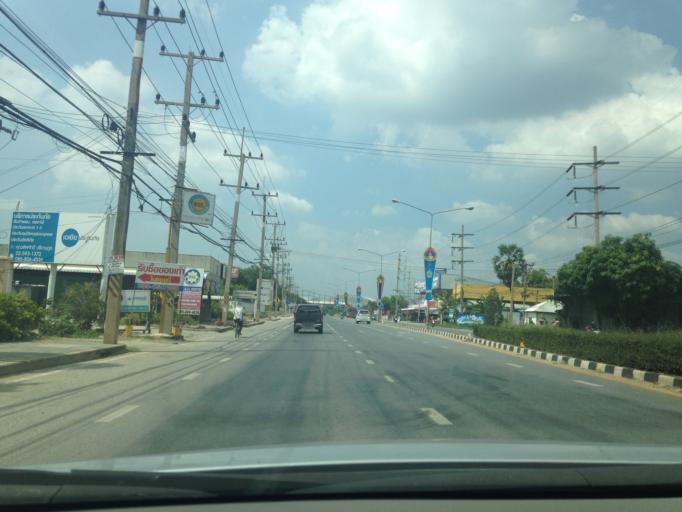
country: TH
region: Pathum Thani
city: Sam Khok
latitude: 14.0693
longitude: 100.5225
